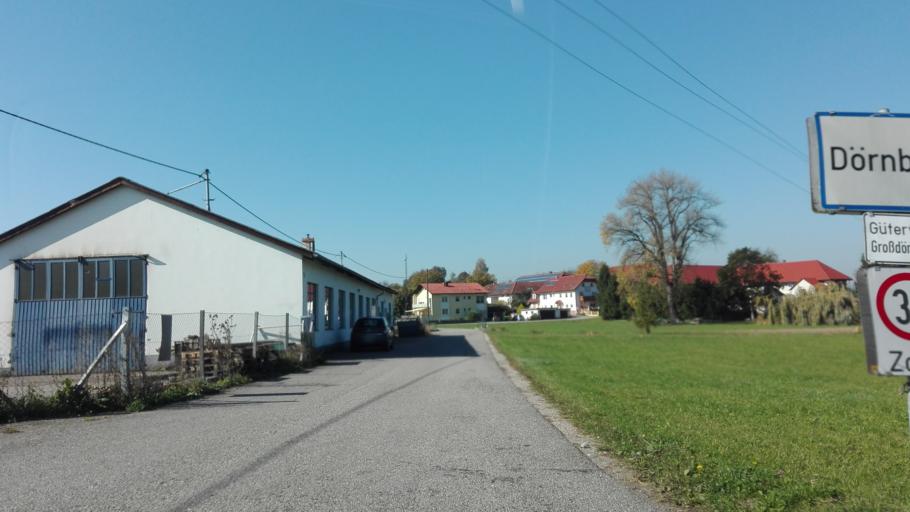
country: AT
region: Upper Austria
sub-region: Politischer Bezirk Linz-Land
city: Pasching
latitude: 48.2859
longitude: 14.1996
